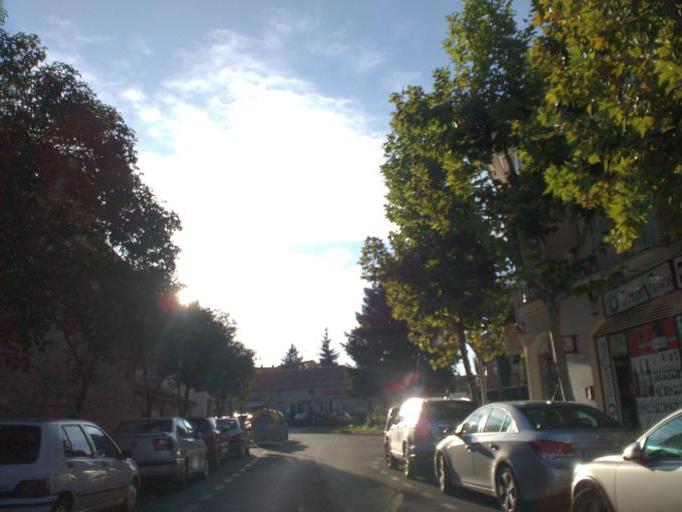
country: ES
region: Madrid
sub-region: Provincia de Madrid
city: Torrelodones
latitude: 40.5766
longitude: -3.9311
